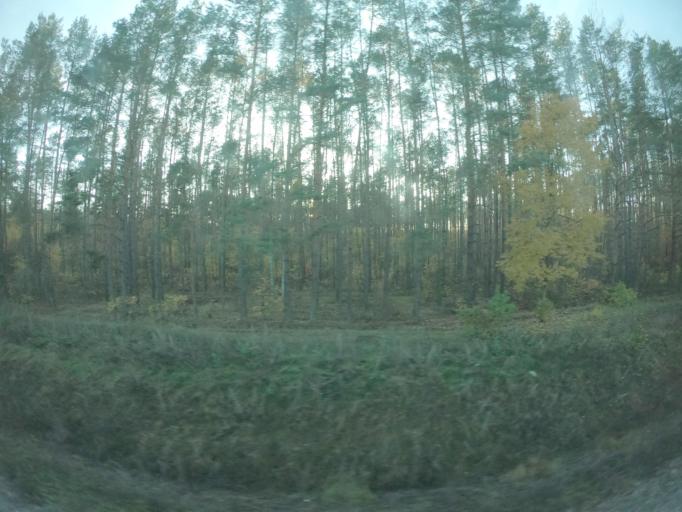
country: PL
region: Lubusz
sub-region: Powiat slubicki
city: Rzepin
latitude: 52.3337
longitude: 14.8353
